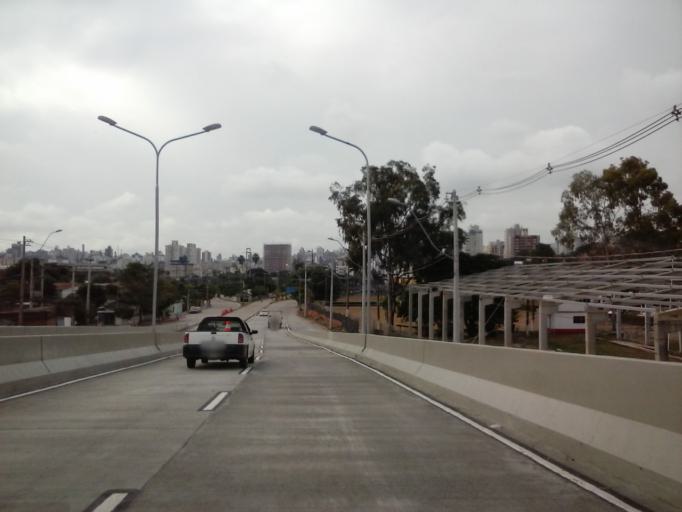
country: BR
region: Rio Grande do Sul
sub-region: Porto Alegre
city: Porto Alegre
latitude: -30.0616
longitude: -51.1849
